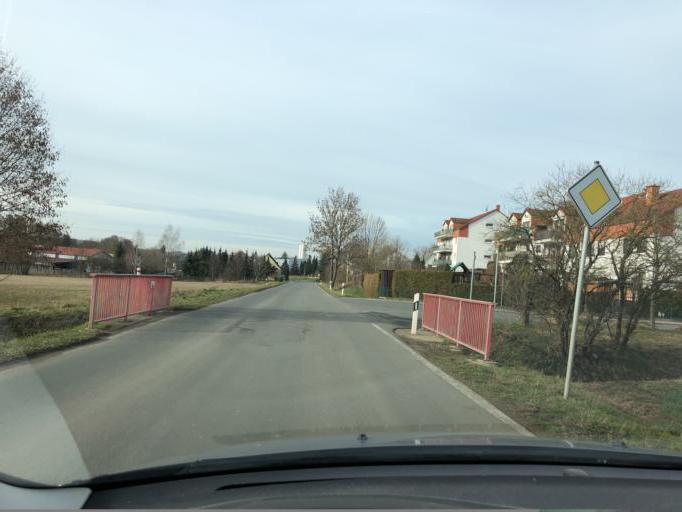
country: DE
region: Saxony-Anhalt
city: Bad Bibra
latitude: 51.2125
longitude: 11.5943
